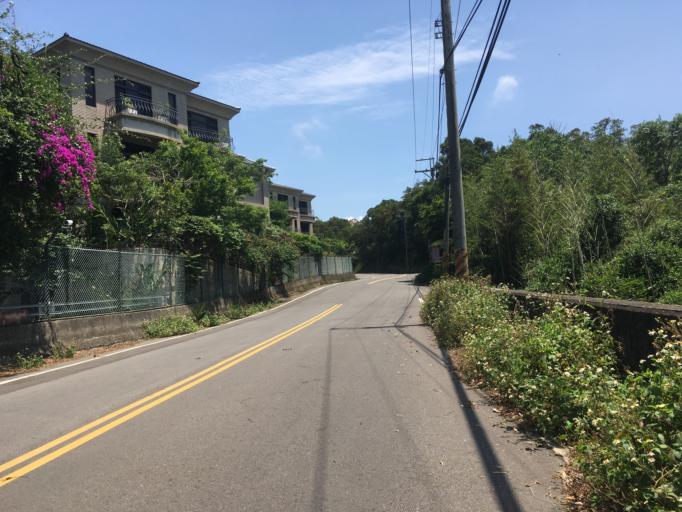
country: TW
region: Taiwan
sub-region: Hsinchu
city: Hsinchu
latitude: 24.7387
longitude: 120.9852
